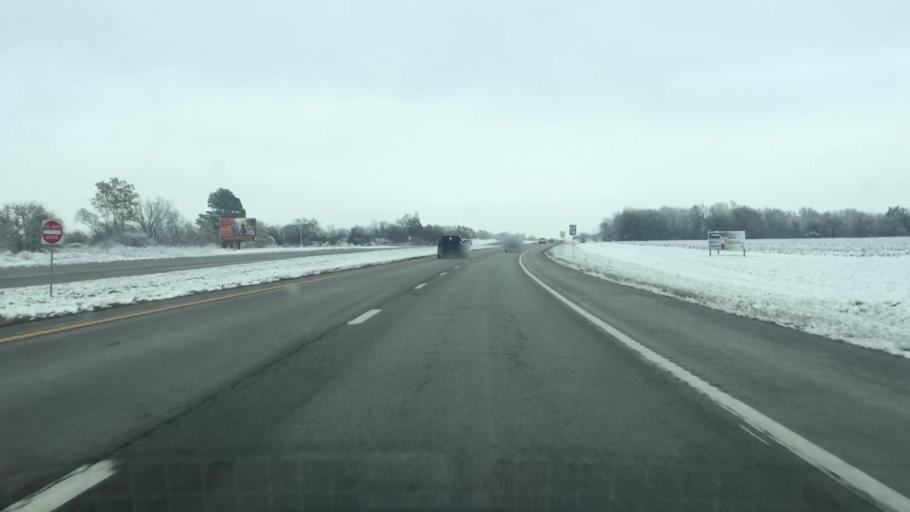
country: US
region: Missouri
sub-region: Cass County
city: Harrisonville
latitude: 38.6091
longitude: -94.3019
